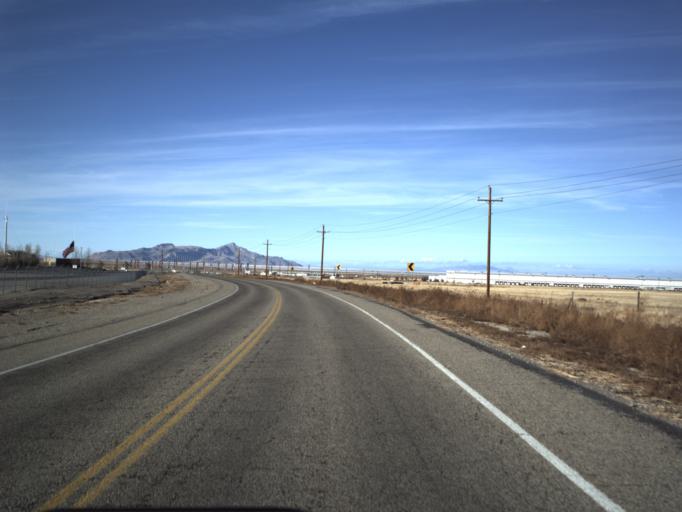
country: US
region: Utah
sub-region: Tooele County
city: Erda
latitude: 40.5782
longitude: -112.3677
